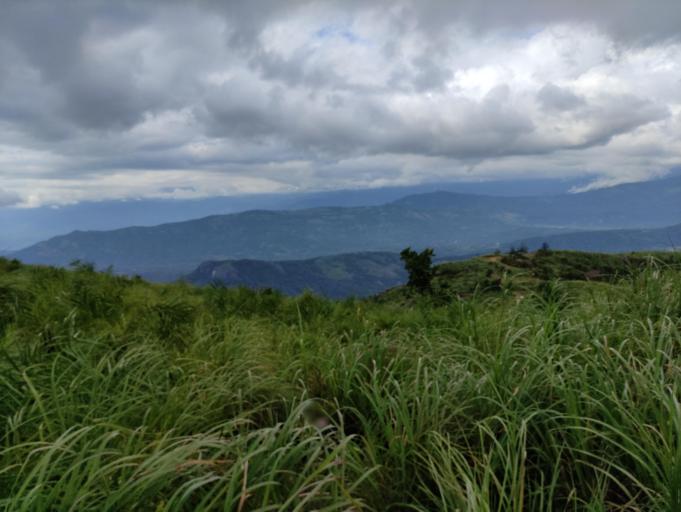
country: IN
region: Kerala
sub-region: Kottayam
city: Erattupetta
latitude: 9.8055
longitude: 76.7829
